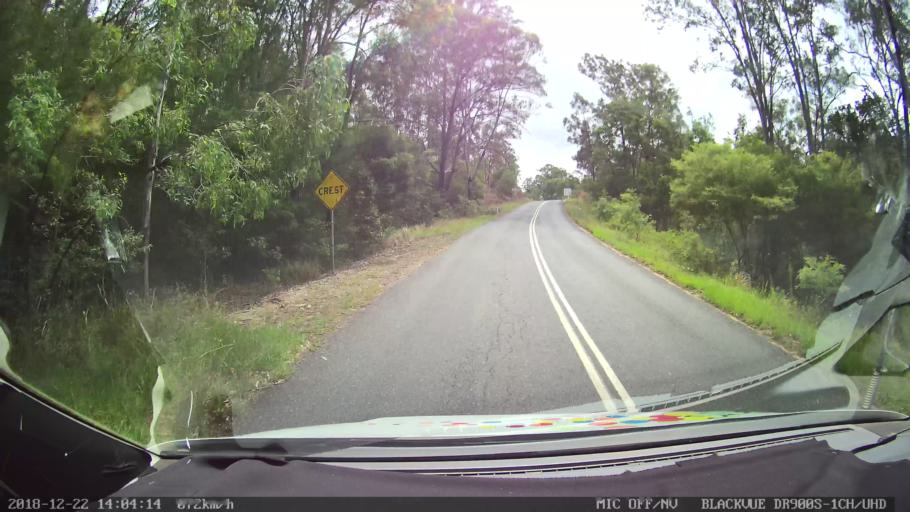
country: AU
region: New South Wales
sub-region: Clarence Valley
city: Coutts Crossing
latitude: -29.9349
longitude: 152.7307
